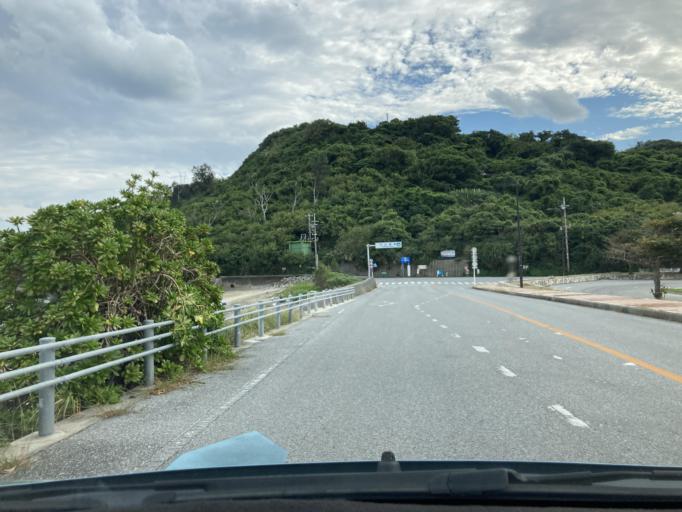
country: JP
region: Okinawa
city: Katsuren-haebaru
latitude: 26.3286
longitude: 127.9571
